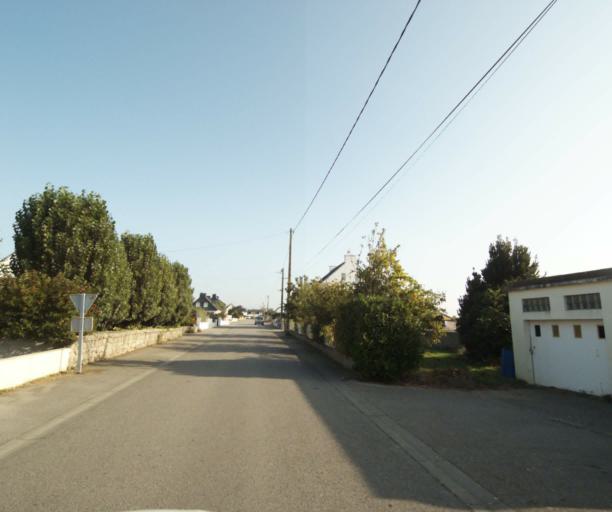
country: FR
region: Brittany
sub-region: Departement du Morbihan
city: Riantec
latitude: 47.7126
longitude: -3.3022
